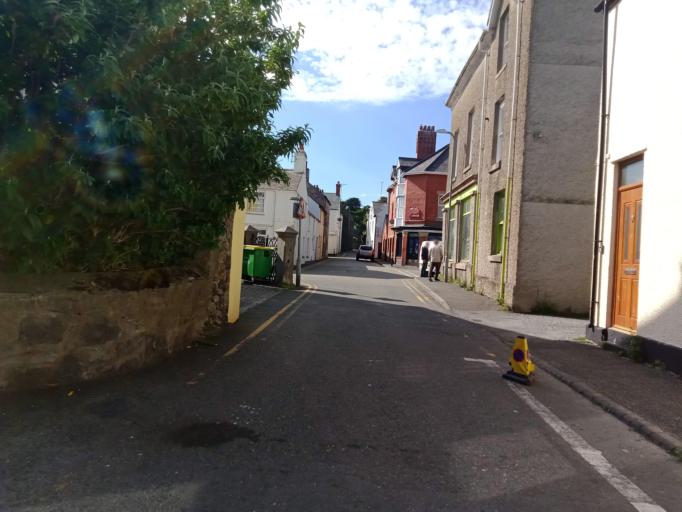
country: GB
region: Wales
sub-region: Anglesey
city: Beaumaris
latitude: 53.2628
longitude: -4.0937
